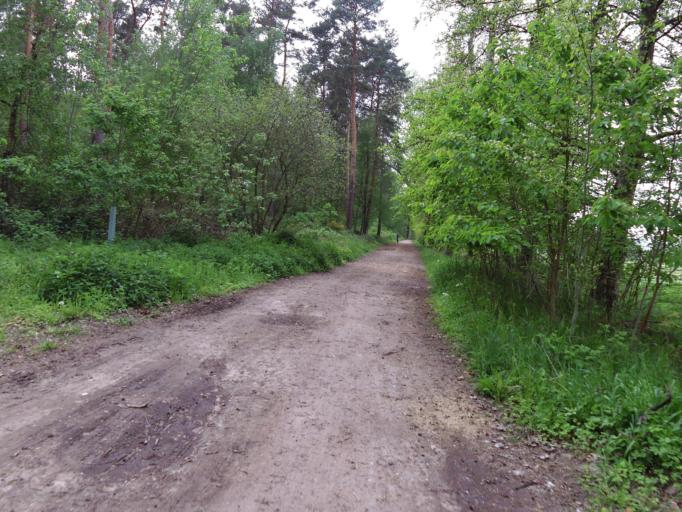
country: DE
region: Rheinland-Pfalz
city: Hassloch
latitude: 49.3494
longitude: 8.2338
